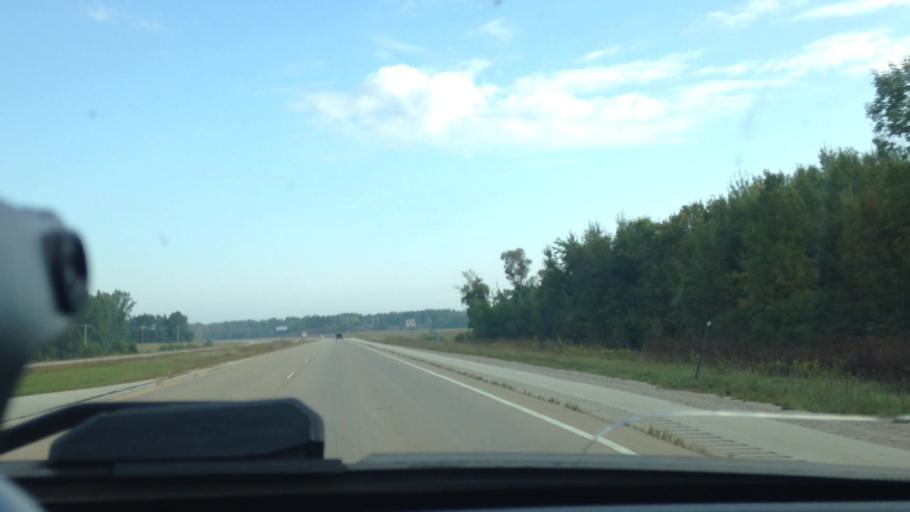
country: US
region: Wisconsin
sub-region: Oconto County
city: Oconto Falls
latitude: 44.9606
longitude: -88.0359
